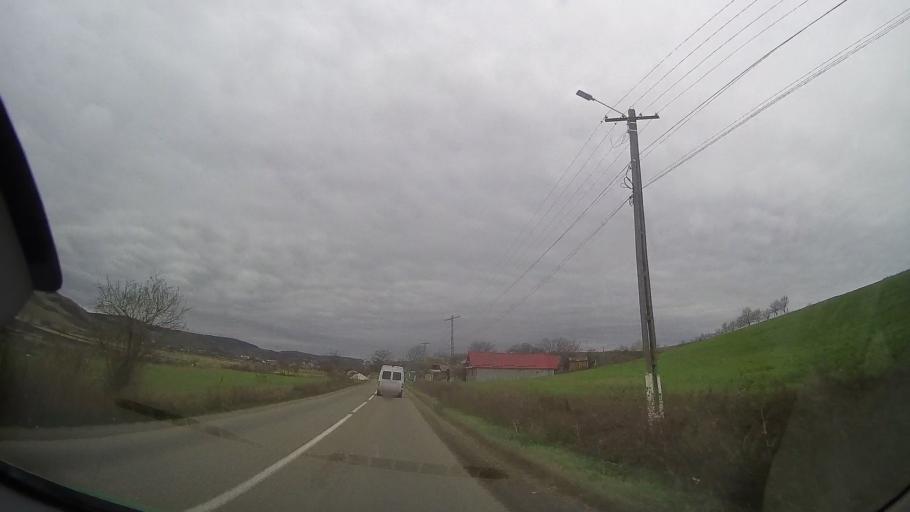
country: RO
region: Mures
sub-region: Comuna Sarmasu
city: Sarmasu
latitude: 46.7938
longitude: 24.2106
